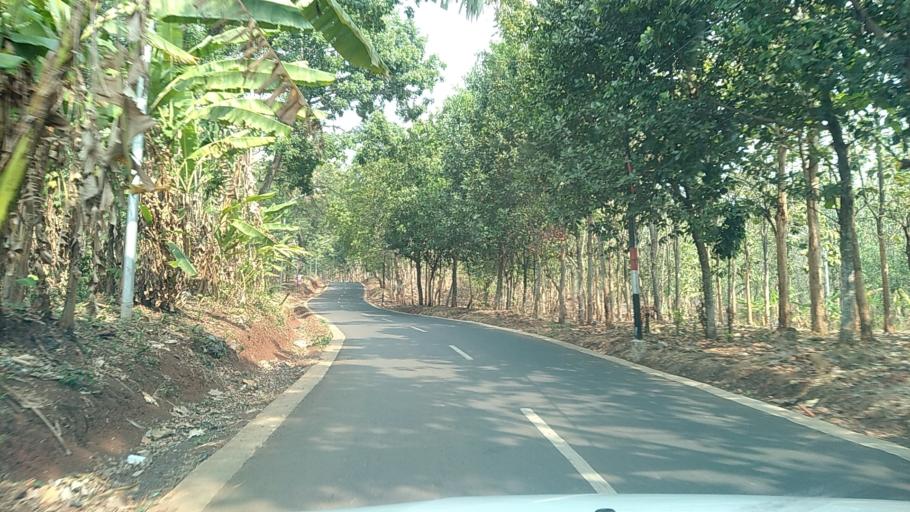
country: ID
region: Central Java
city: Semarang
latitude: -6.9999
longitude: 110.3023
